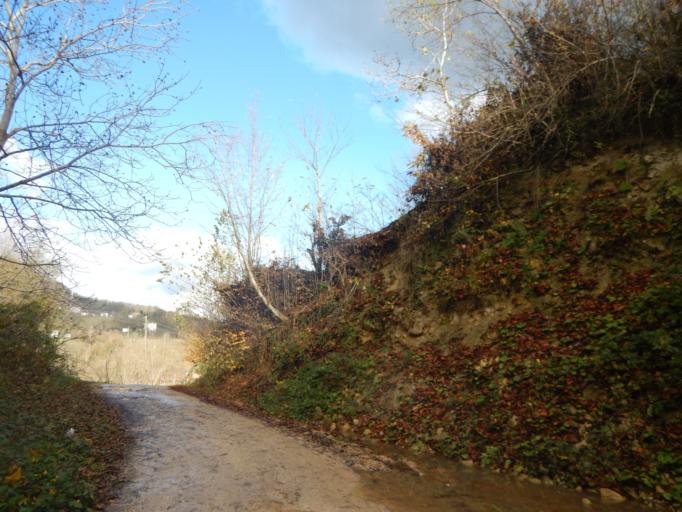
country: TR
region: Ordu
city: Kumru
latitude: 40.9346
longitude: 37.3051
